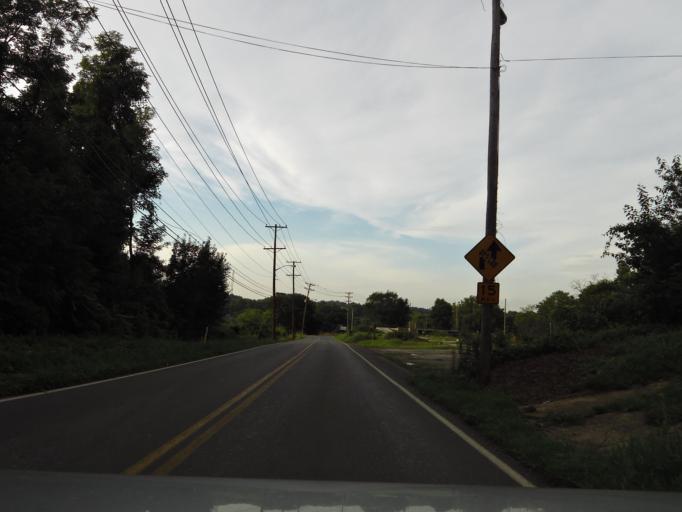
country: US
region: Tennessee
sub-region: Knox County
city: Knoxville
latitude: 35.9328
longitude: -83.9172
